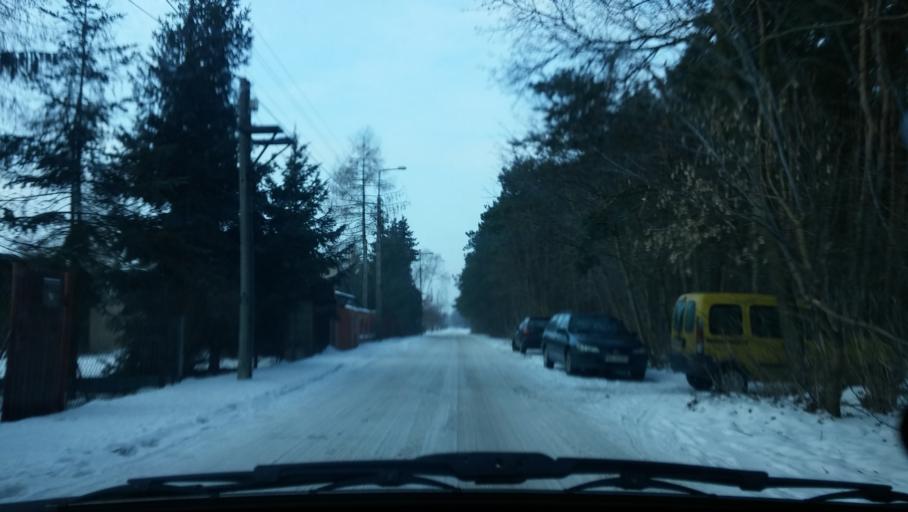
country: PL
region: Masovian Voivodeship
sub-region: Powiat otwocki
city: Jozefow
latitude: 52.1551
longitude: 21.1991
